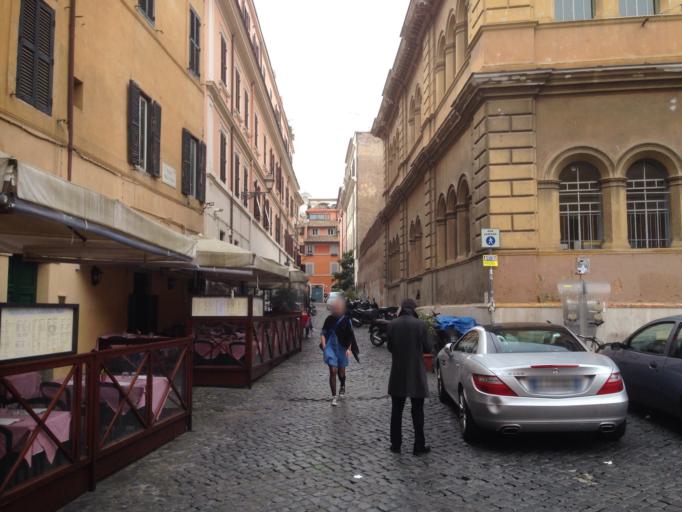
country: VA
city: Vatican City
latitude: 41.8910
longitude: 12.4683
